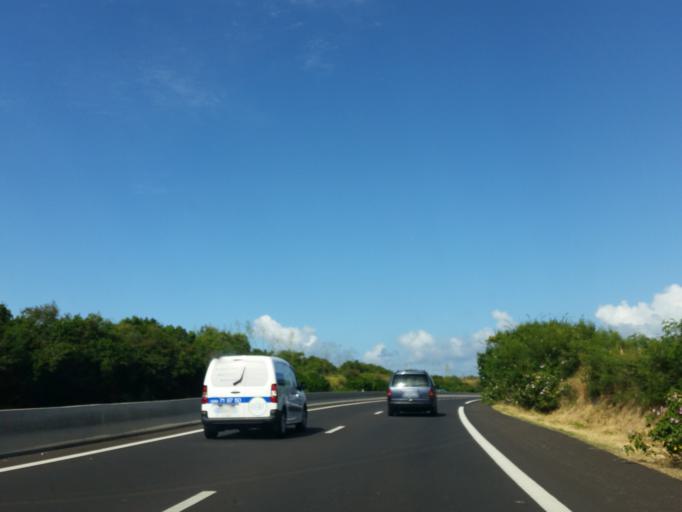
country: RE
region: Reunion
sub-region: Reunion
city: Saint-Pierre
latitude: -21.3179
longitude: 55.4446
